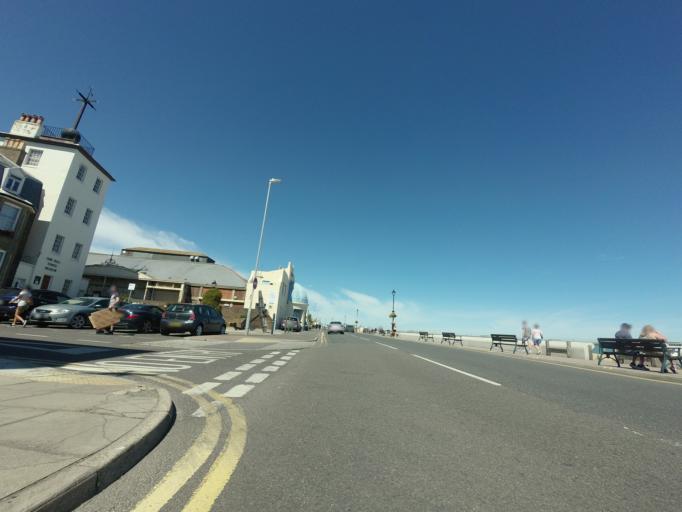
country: GB
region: England
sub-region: Kent
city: Deal
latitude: 51.2217
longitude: 1.4048
